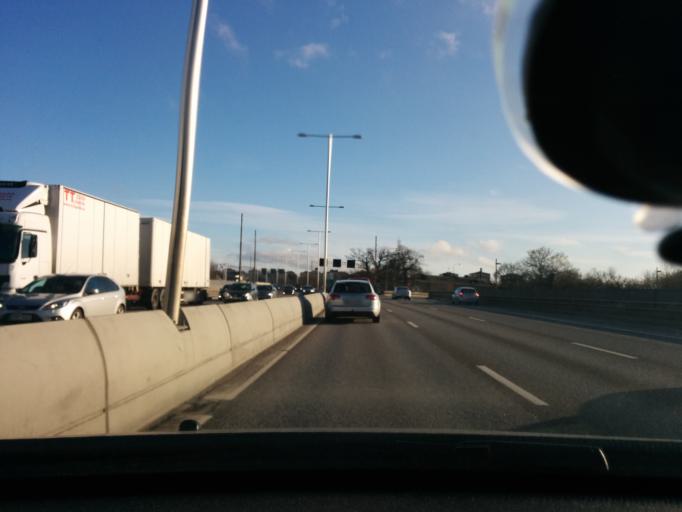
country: SE
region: Stockholm
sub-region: Solna Kommun
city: Solna
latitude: 59.3354
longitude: 18.0100
